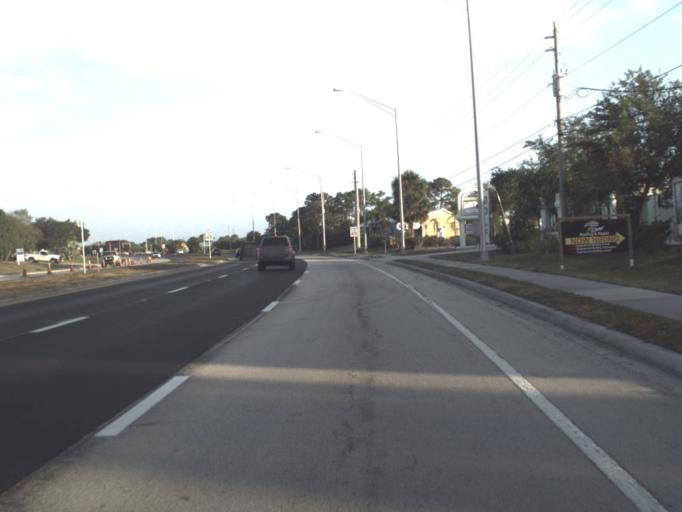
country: US
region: Florida
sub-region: Brevard County
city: Indian Harbour Beach
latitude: 28.1521
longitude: -80.6405
